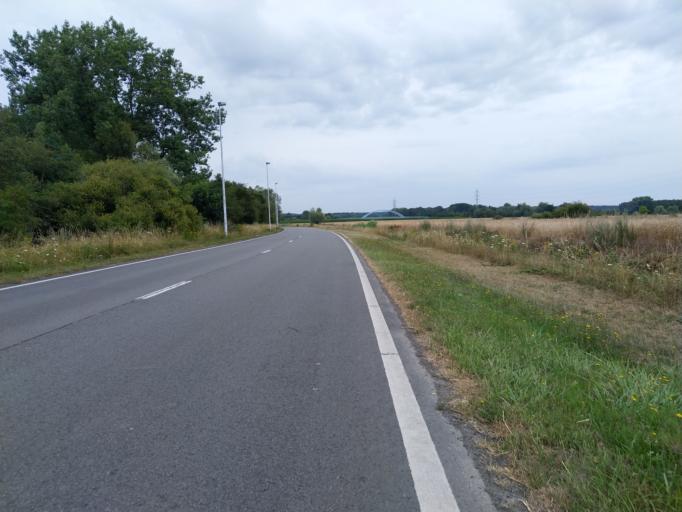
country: BE
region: Wallonia
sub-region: Province du Hainaut
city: Hensies
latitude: 50.4582
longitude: 3.7001
